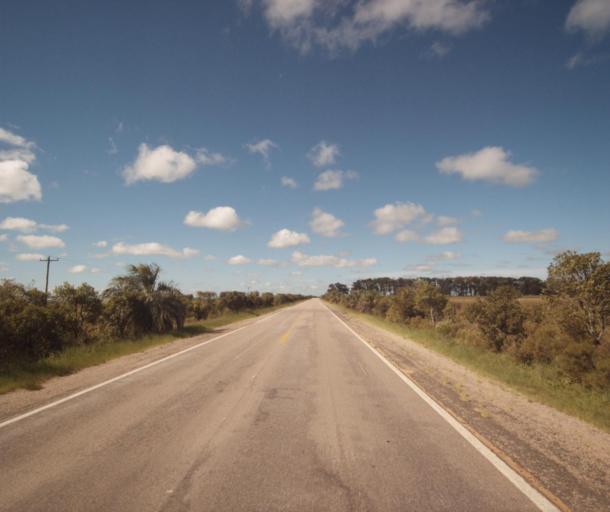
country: BR
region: Rio Grande do Sul
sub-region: Santa Vitoria Do Palmar
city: Santa Vitoria do Palmar
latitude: -33.4103
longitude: -53.2287
